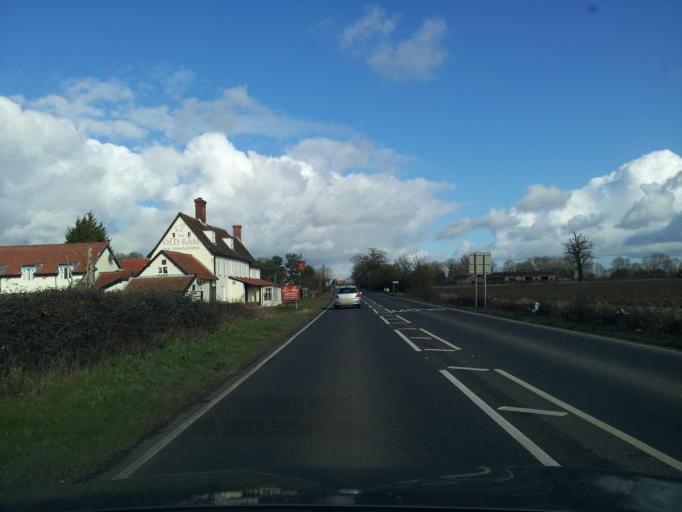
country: GB
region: England
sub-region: Norfolk
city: Long Stratton
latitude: 52.4226
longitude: 1.2023
